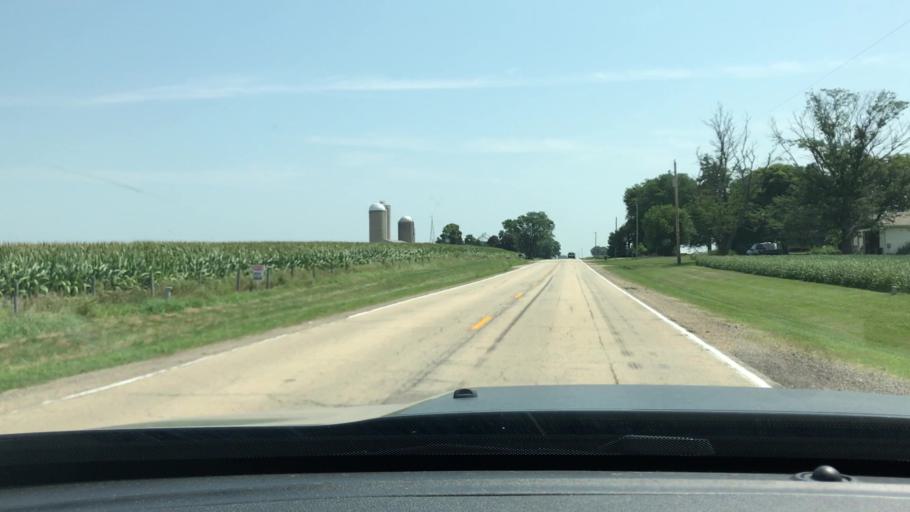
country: US
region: Illinois
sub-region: LaSalle County
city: Earlville
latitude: 41.4691
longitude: -88.9192
